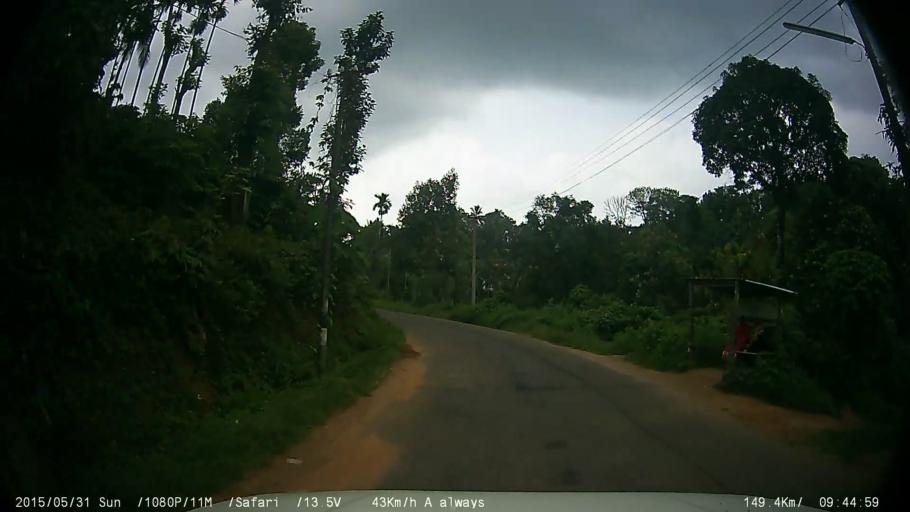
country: IN
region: Kerala
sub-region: Wayanad
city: Kalpetta
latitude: 11.6283
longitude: 76.0177
